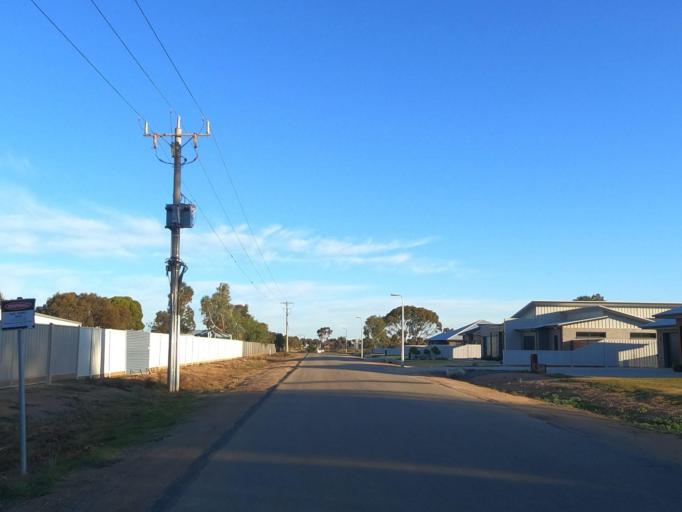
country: AU
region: Victoria
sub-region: Swan Hill
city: Swan Hill
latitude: -35.3315
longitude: 143.5344
